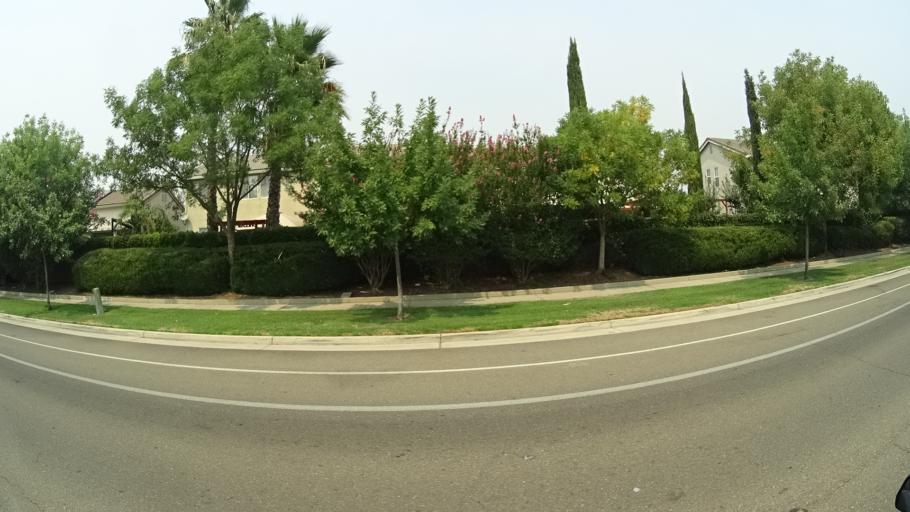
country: US
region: California
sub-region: Sacramento County
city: Laguna
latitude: 38.3995
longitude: -121.4370
